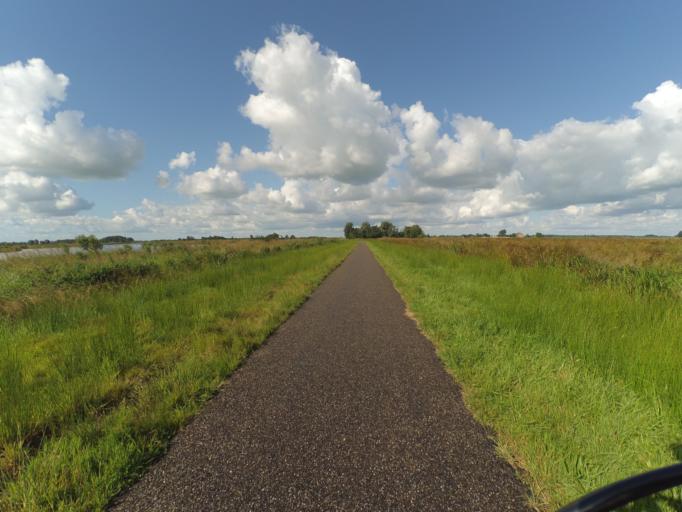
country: NL
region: Friesland
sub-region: Gemeente Dantumadiel
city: Feanwalden
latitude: 53.2525
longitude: 5.9795
